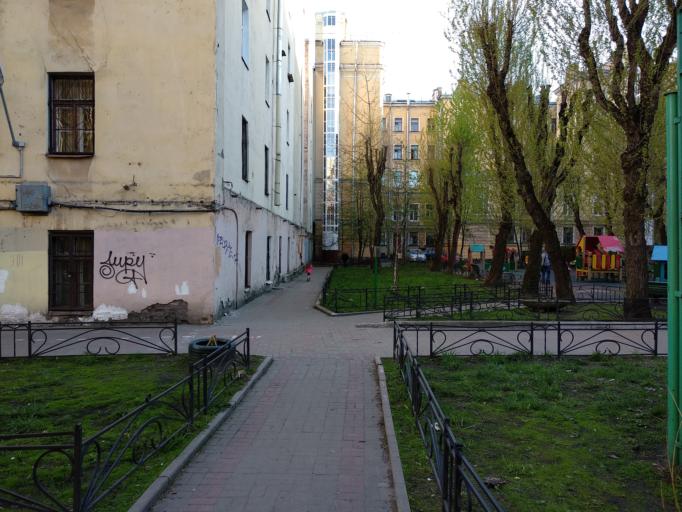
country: RU
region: St.-Petersburg
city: Centralniy
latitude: 59.9280
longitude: 30.3404
